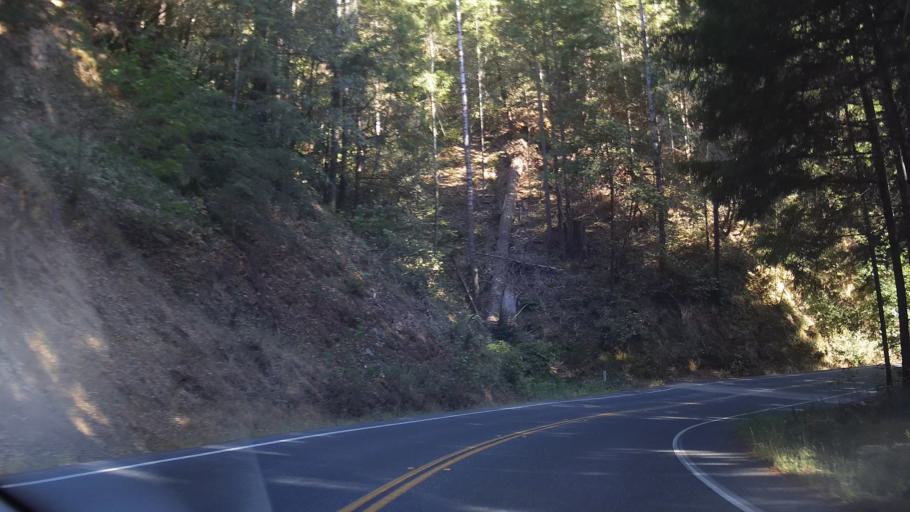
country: US
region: California
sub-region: Mendocino County
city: Brooktrails
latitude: 39.3664
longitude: -123.4986
